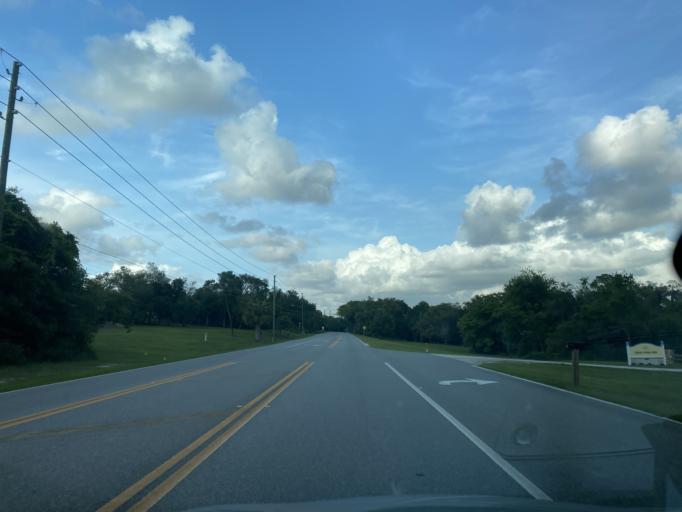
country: US
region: Florida
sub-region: Volusia County
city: DeBary
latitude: 28.8675
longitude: -81.3117
